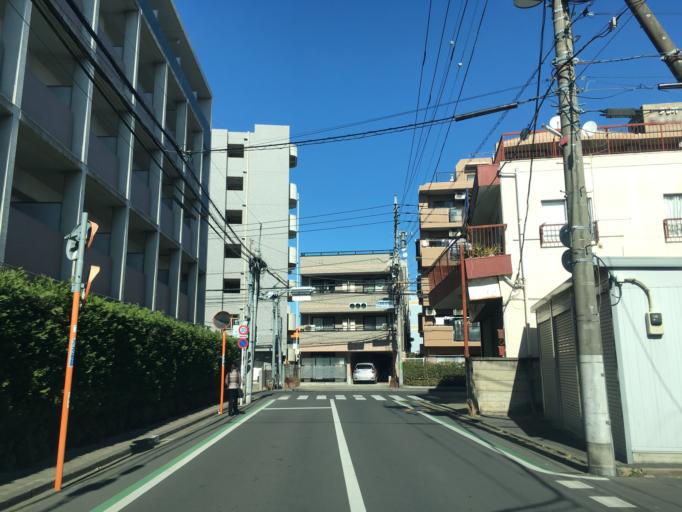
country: JP
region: Tokyo
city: Mitaka-shi
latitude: 35.6834
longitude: 139.5610
